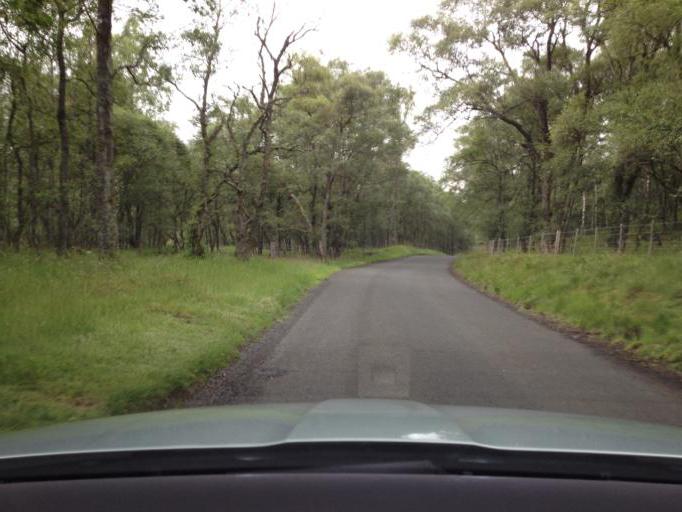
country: GB
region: Scotland
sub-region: Aberdeenshire
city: Aboyne
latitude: 56.8965
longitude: -2.8700
